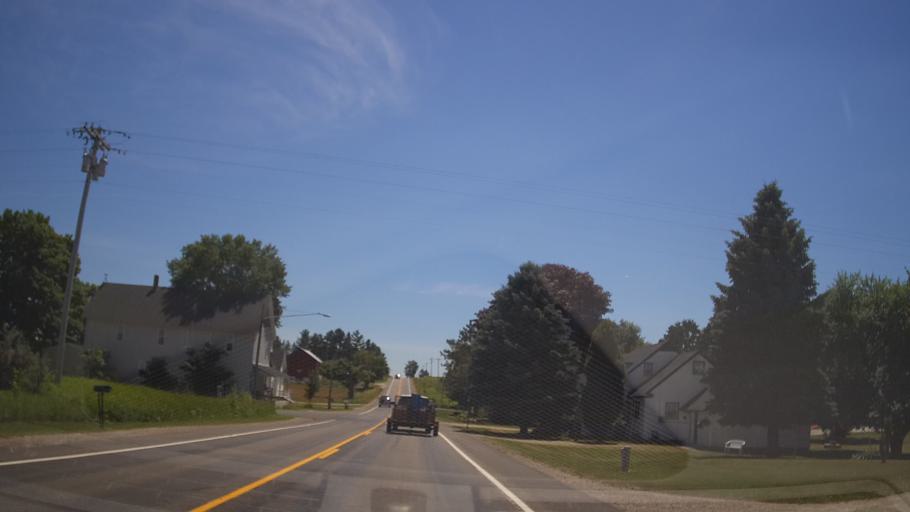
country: US
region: Michigan
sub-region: Grand Traverse County
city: Kingsley
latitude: 44.6147
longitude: -85.6966
